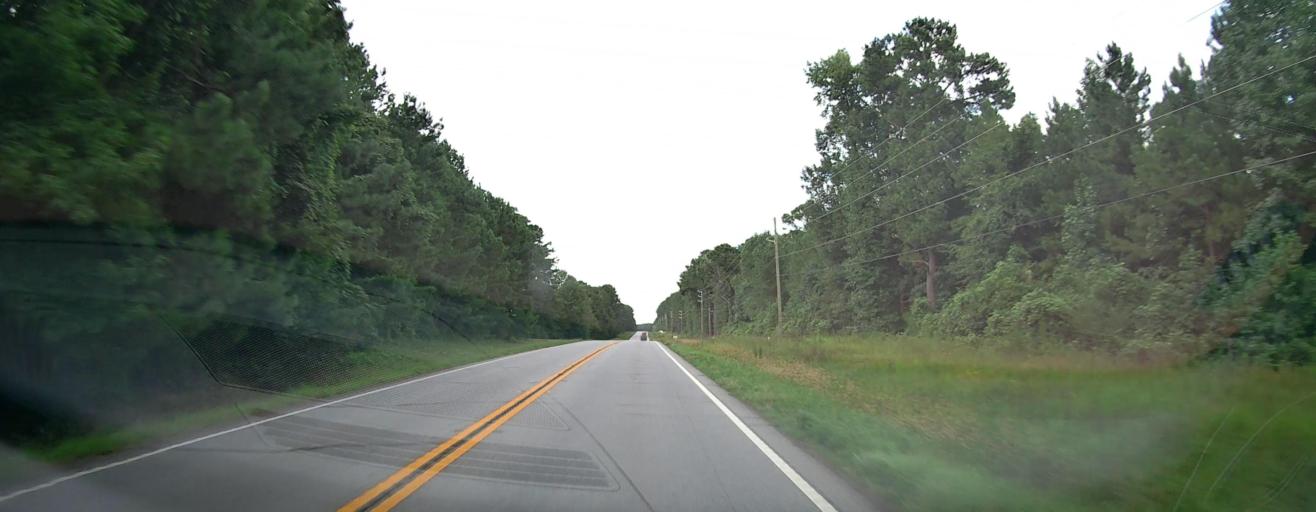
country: US
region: Georgia
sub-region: Meriwether County
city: Greenville
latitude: 33.0721
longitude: -84.5720
